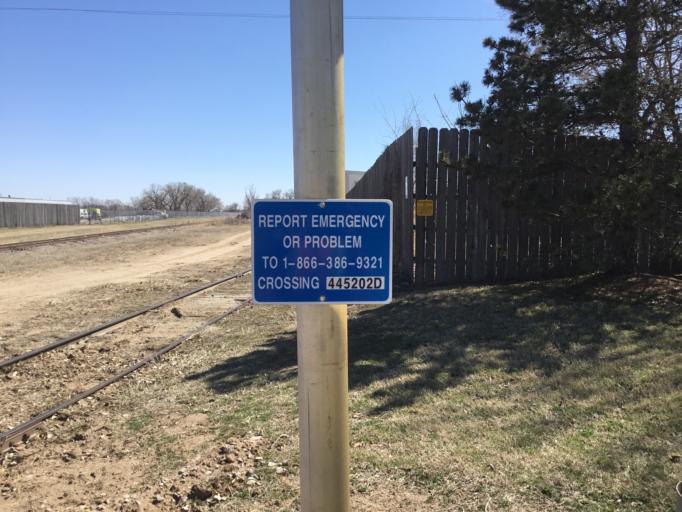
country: US
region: Kansas
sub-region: Sedgwick County
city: Maize
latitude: 37.7306
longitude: -97.4170
